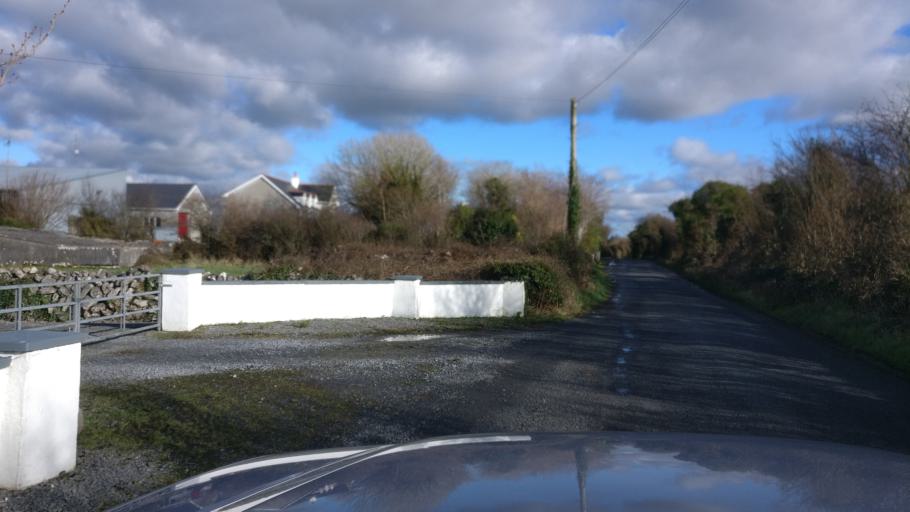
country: IE
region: Connaught
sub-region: County Galway
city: Athenry
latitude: 53.2385
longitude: -8.8048
